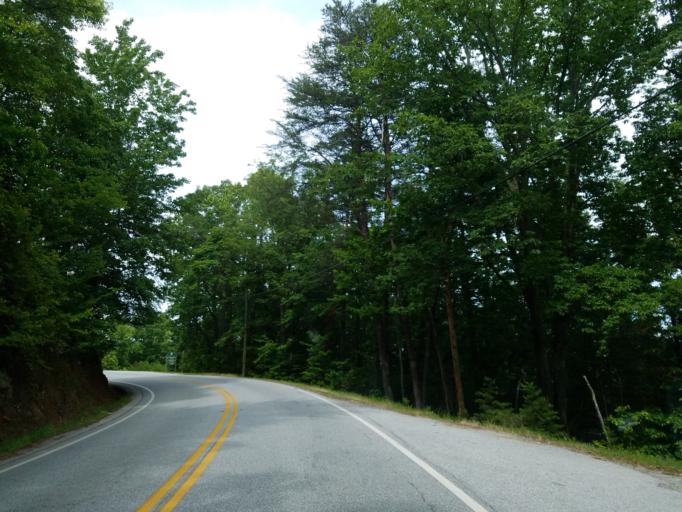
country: US
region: Georgia
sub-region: Lumpkin County
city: Dahlonega
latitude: 34.6111
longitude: -83.9644
